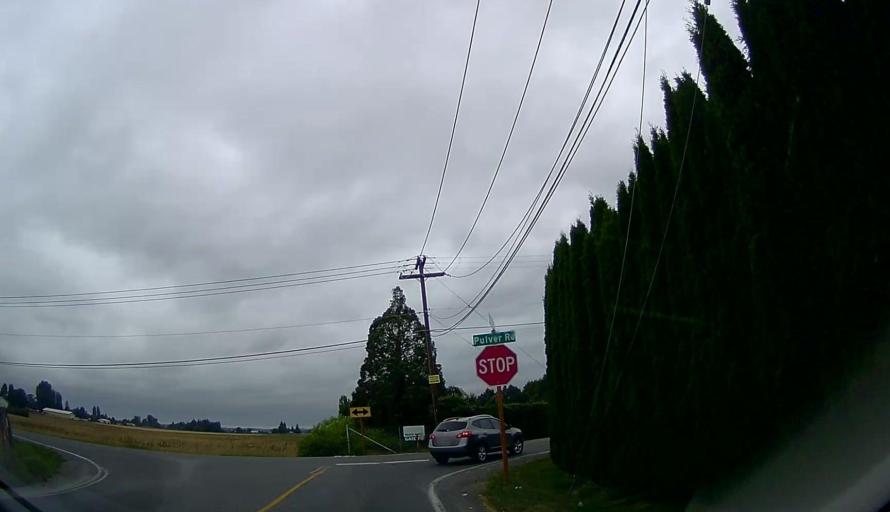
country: US
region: Washington
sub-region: Skagit County
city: Burlington
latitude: 48.4542
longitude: -122.3567
